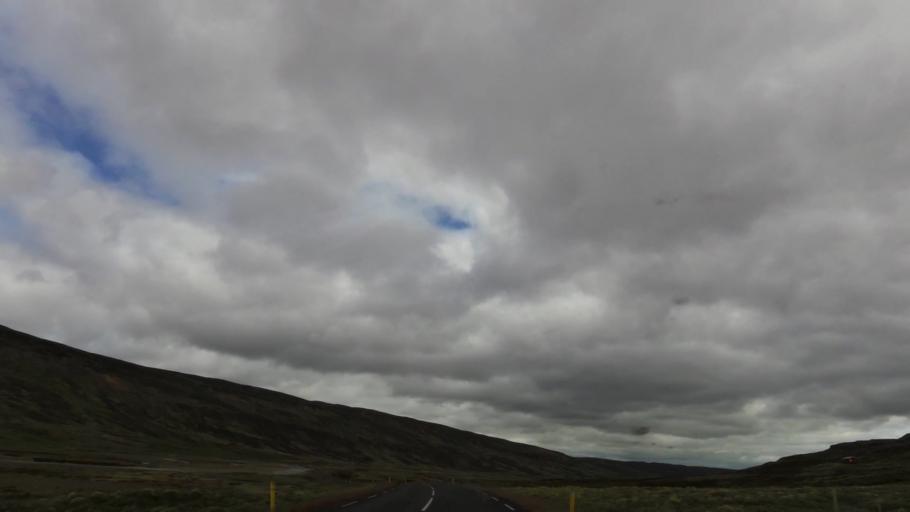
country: IS
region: West
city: Stykkisholmur
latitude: 65.7605
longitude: -21.8435
